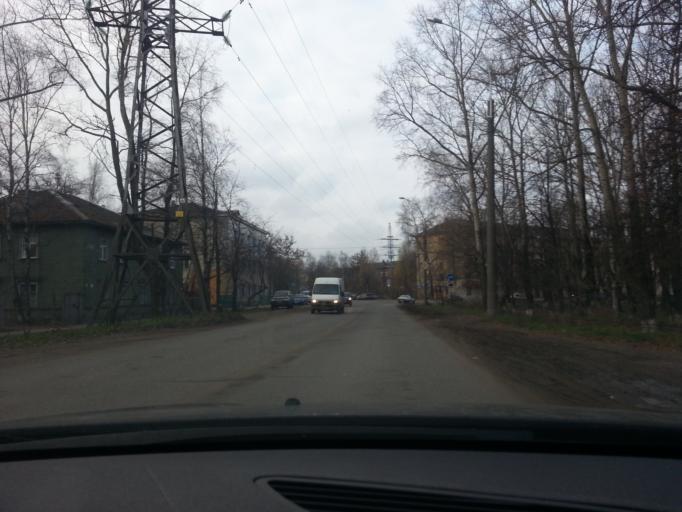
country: RU
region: Vologda
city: Vologda
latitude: 59.2275
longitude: 39.9158
